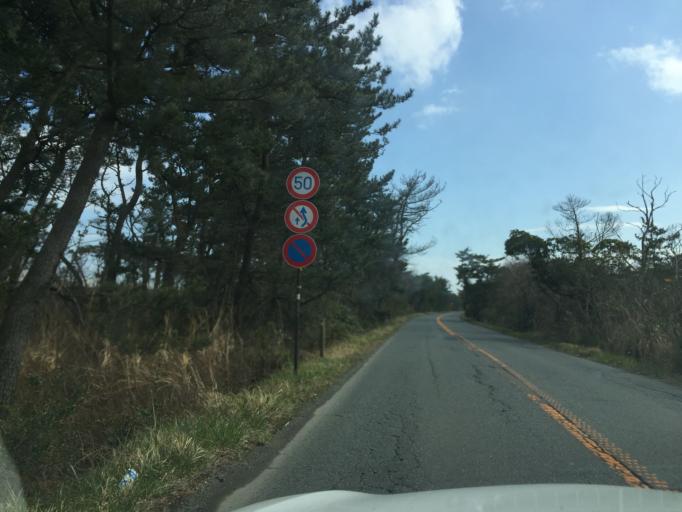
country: JP
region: Fukushima
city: Iwaki
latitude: 37.0473
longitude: 140.9723
